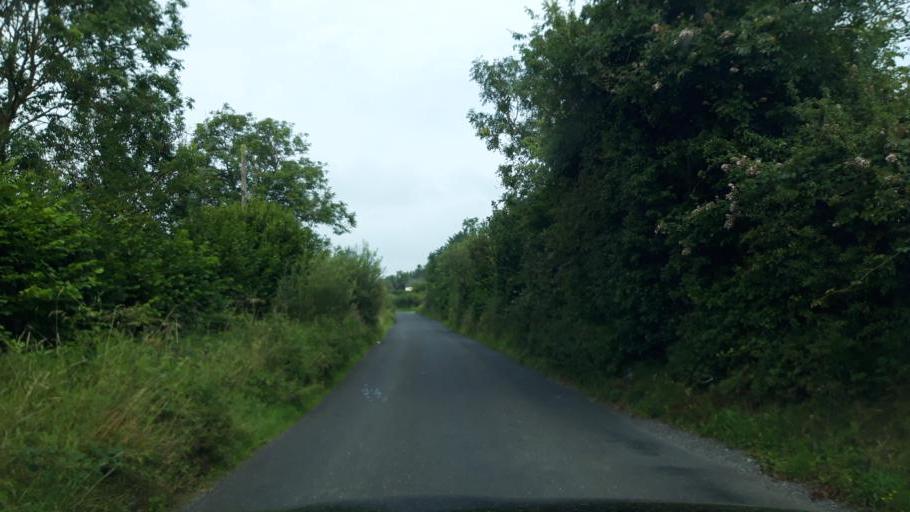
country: IE
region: Munster
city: Fethard
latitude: 52.5833
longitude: -7.5898
